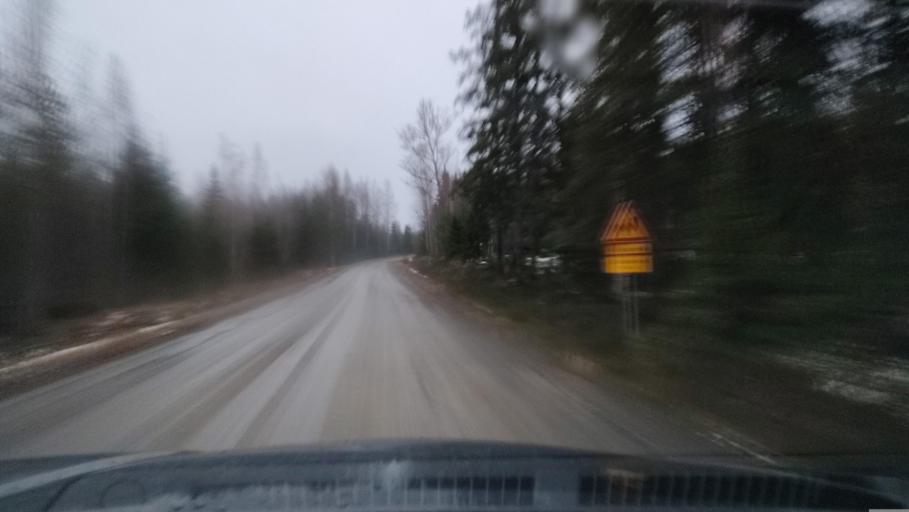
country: FI
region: Southern Ostrobothnia
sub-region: Suupohja
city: Karijoki
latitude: 62.1286
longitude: 21.6117
